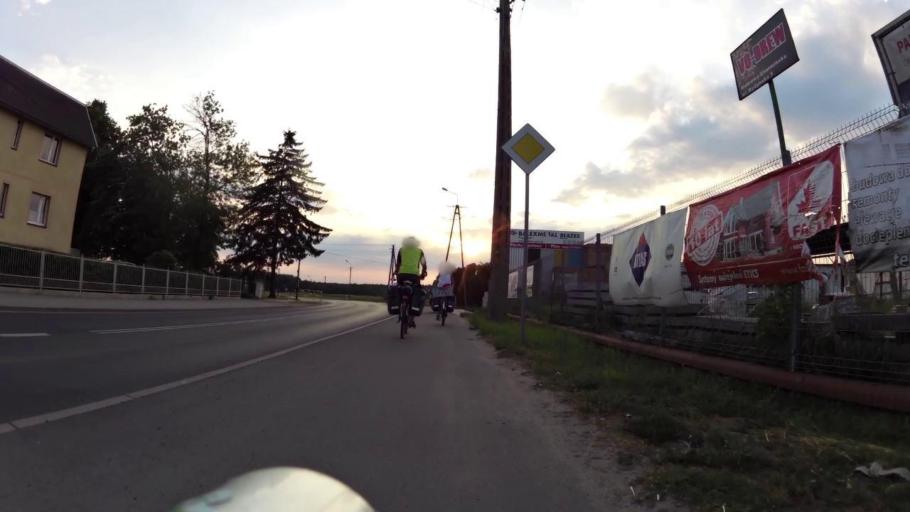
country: PL
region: Kujawsko-Pomorskie
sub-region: Powiat bydgoski
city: Dabrowa Chelminska
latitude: 53.1789
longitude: 18.2952
